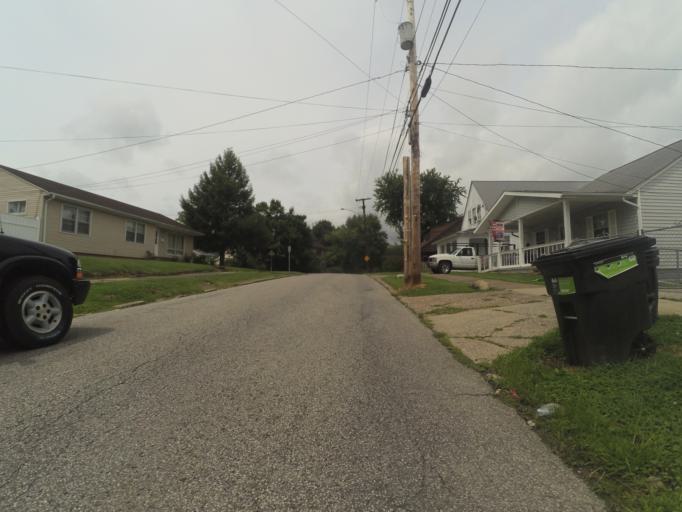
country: US
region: West Virginia
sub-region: Cabell County
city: Huntington
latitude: 38.4117
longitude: -82.4089
